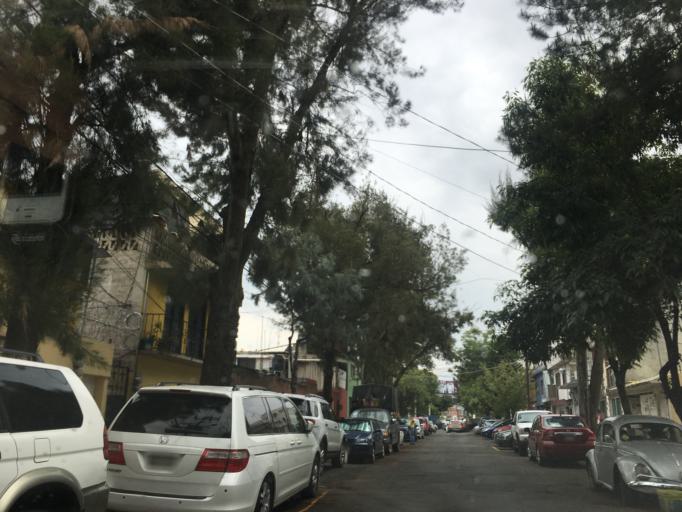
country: MX
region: Mexico City
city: Magdalena Contreras
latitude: 19.3422
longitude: -99.2009
